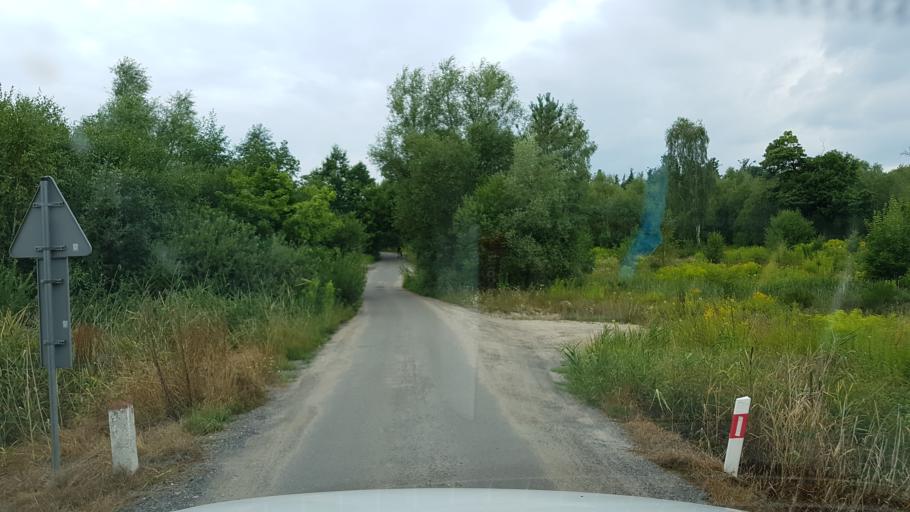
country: PL
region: West Pomeranian Voivodeship
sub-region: Powiat szczecinecki
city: Szczecinek
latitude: 53.6830
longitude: 16.6955
